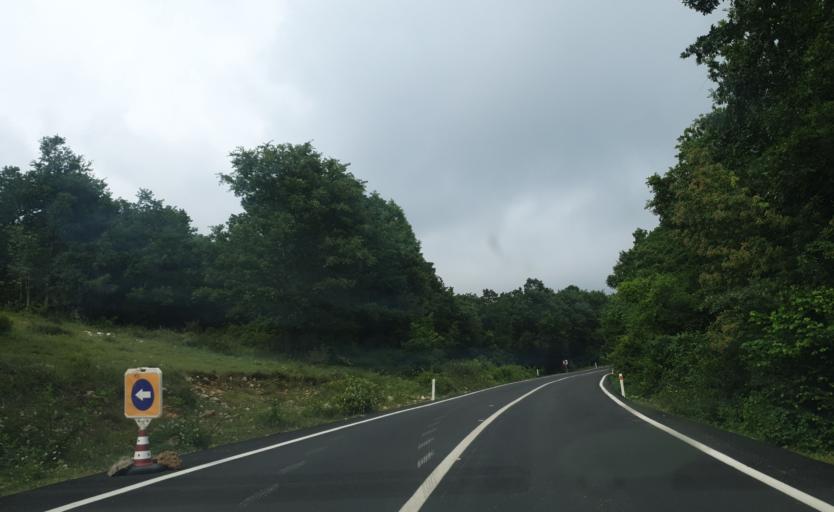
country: TR
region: Kirklareli
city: Salmydessus
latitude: 41.5880
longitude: 28.0677
